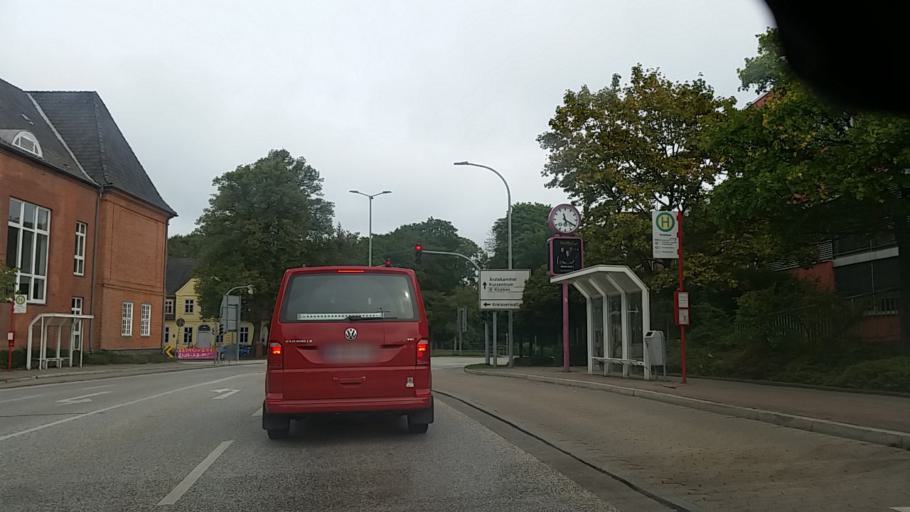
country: DE
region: Schleswig-Holstein
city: Bad Segeberg
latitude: 53.9361
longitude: 10.3043
